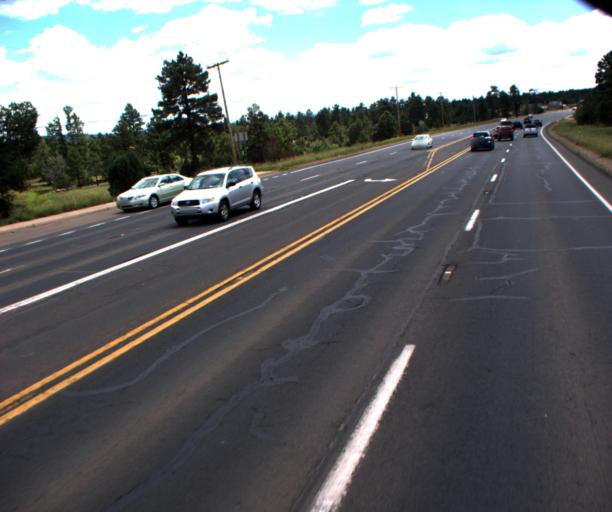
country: US
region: Arizona
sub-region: Navajo County
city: Lake of the Woods
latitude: 34.1962
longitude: -110.0168
